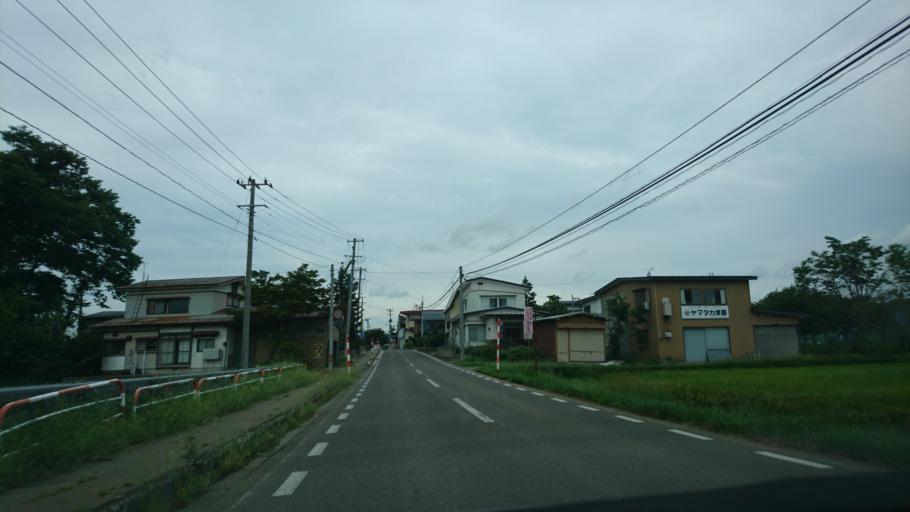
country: JP
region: Akita
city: Yuzawa
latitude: 39.1745
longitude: 140.5561
